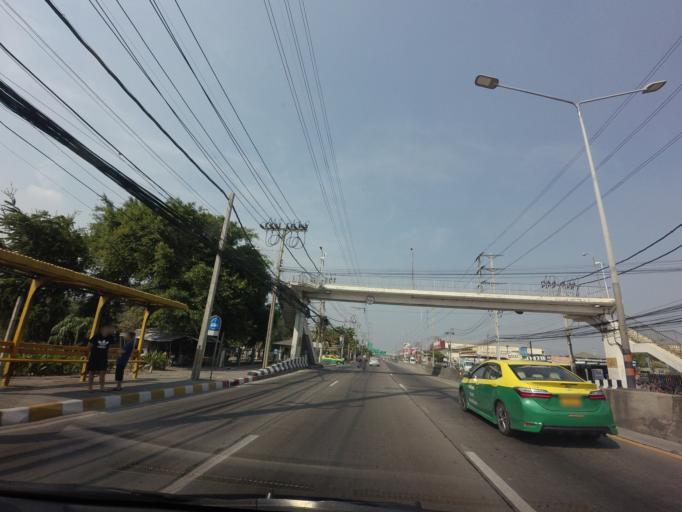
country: TH
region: Bangkok
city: Lat Krabang
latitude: 13.7512
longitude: 100.7464
